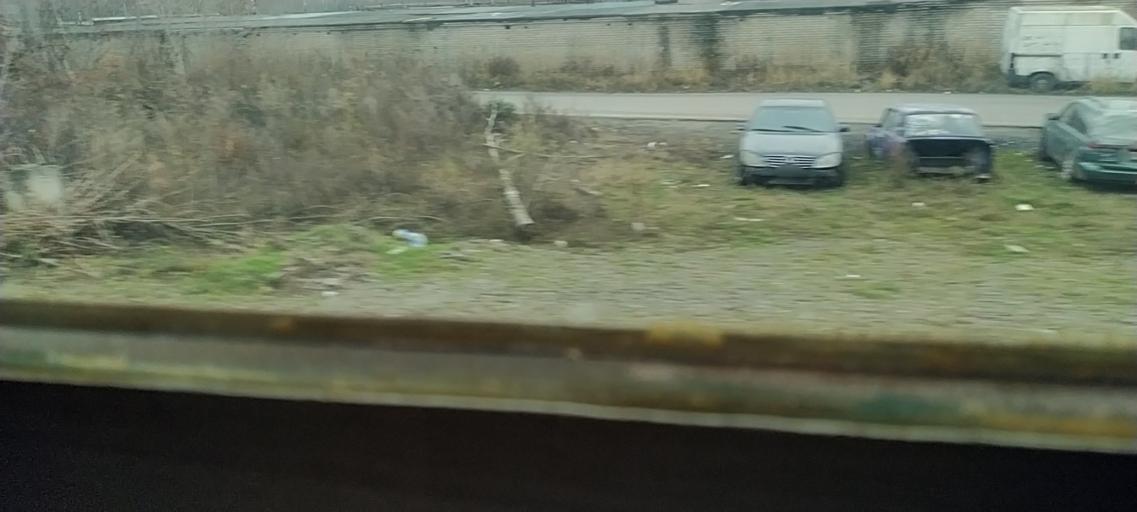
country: RU
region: Moskovskaya
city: Korenevo
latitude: 55.6690
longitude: 37.9910
